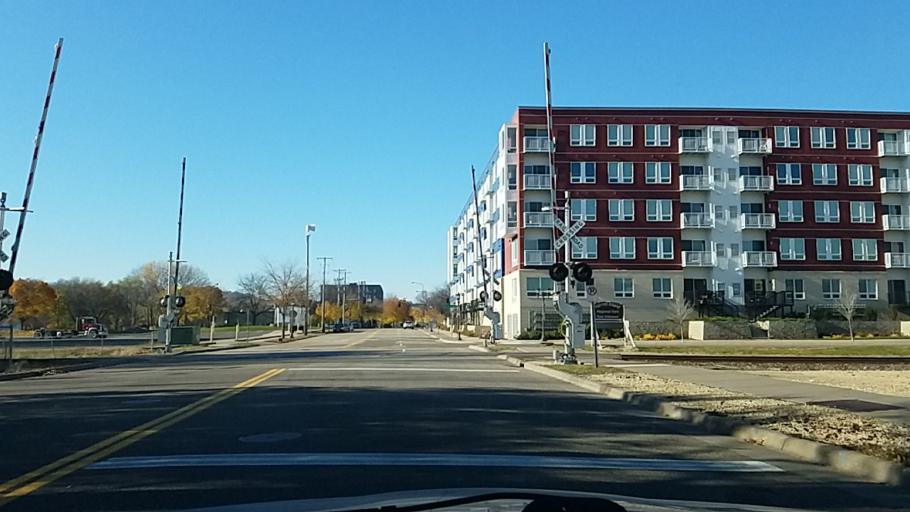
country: US
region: Minnesota
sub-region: Ramsey County
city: Saint Paul
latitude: 44.9402
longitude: -93.0877
